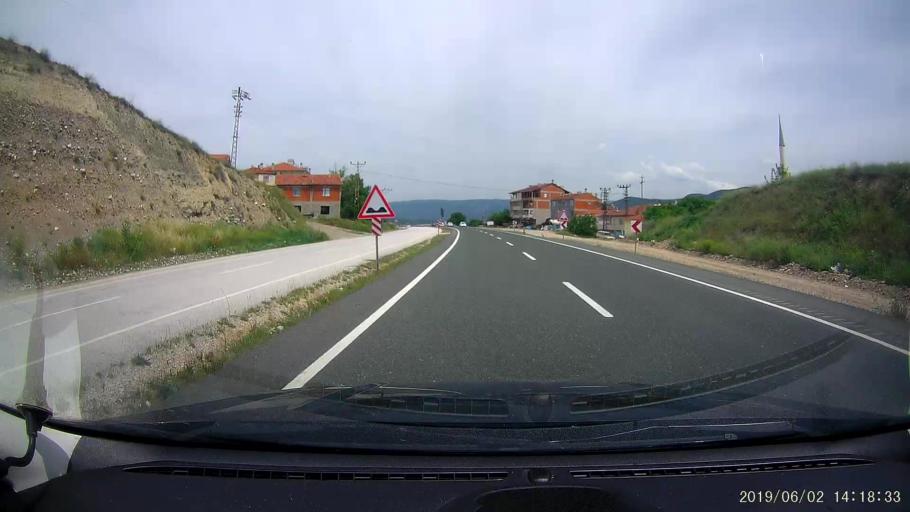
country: TR
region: Kastamonu
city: Tosya
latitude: 40.9564
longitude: 33.9580
